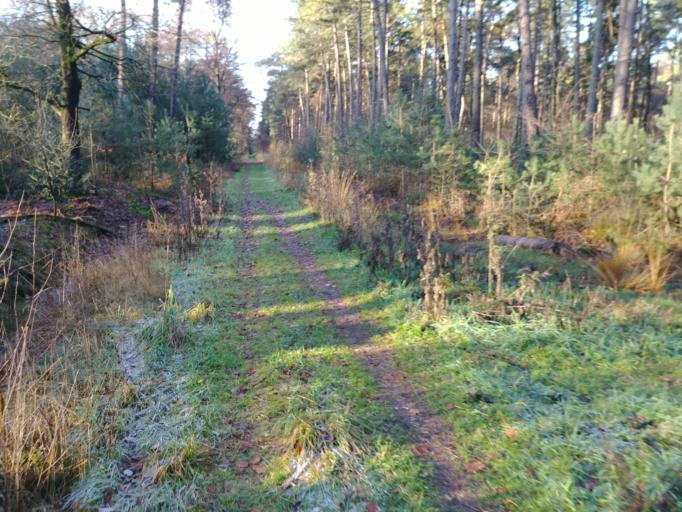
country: NL
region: Utrecht
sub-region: Gemeente Utrechtse Heuvelrug
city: Maarn
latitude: 52.0436
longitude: 5.3729
